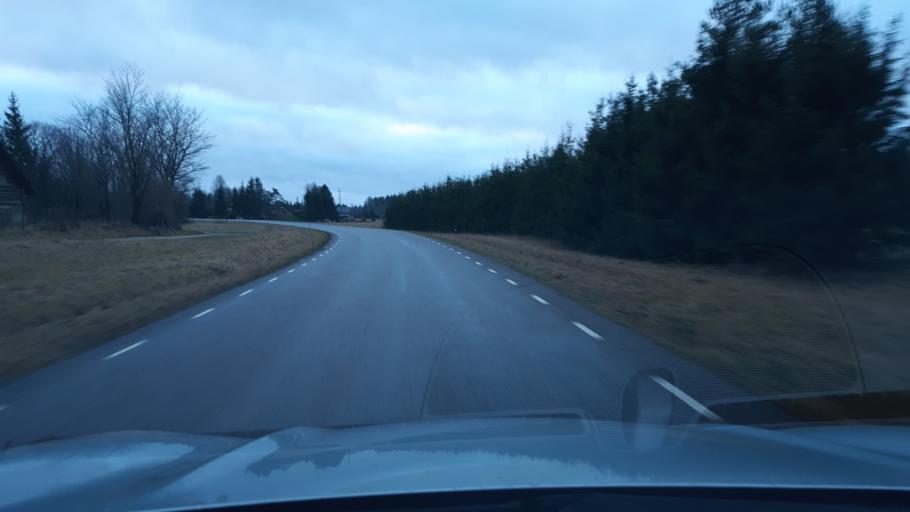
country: EE
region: Raplamaa
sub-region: Kohila vald
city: Kohila
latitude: 59.1012
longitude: 24.6757
